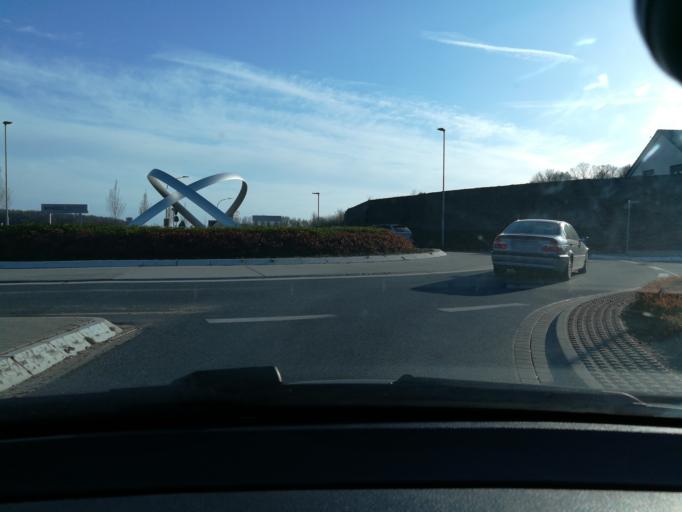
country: DE
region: North Rhine-Westphalia
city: Borgholzhausen
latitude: 52.0944
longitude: 8.2905
